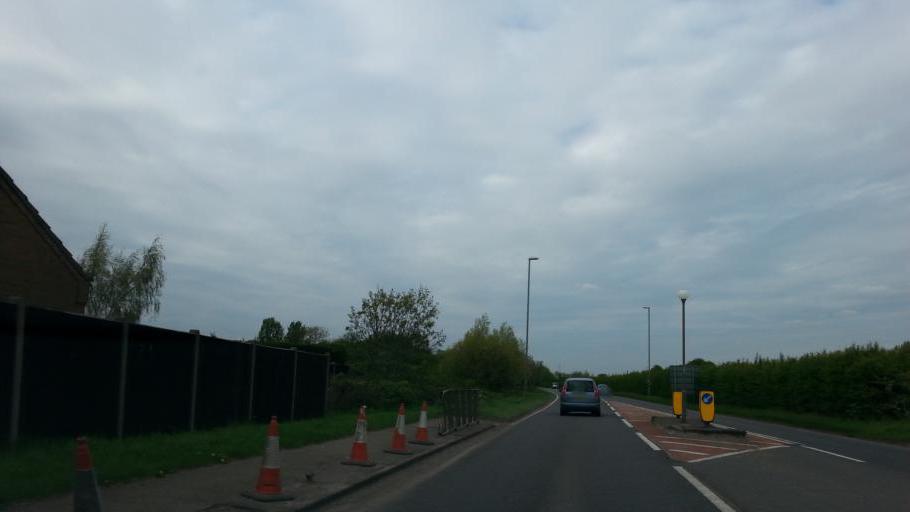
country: GB
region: England
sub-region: Cambridgeshire
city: Doddington
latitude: 52.5130
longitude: 0.0892
